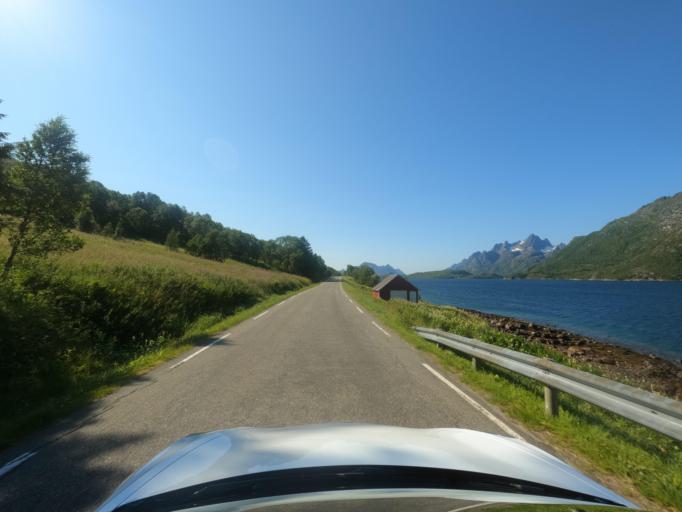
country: NO
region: Nordland
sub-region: Hadsel
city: Stokmarknes
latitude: 68.3815
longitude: 15.0888
